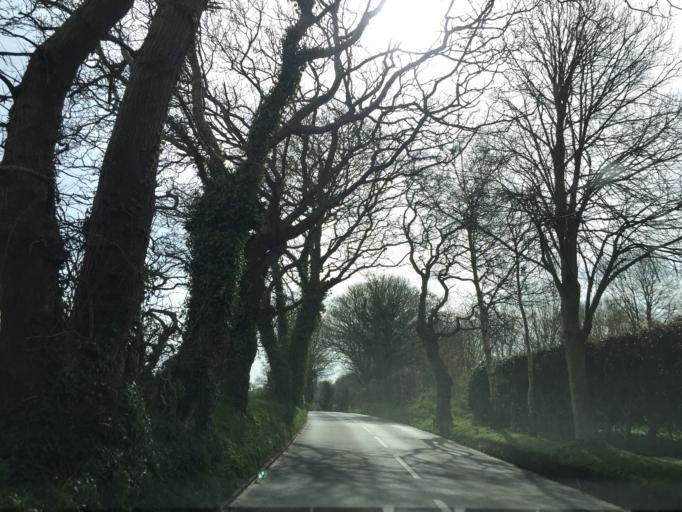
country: JE
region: St Helier
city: Saint Helier
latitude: 49.2307
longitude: -2.0755
